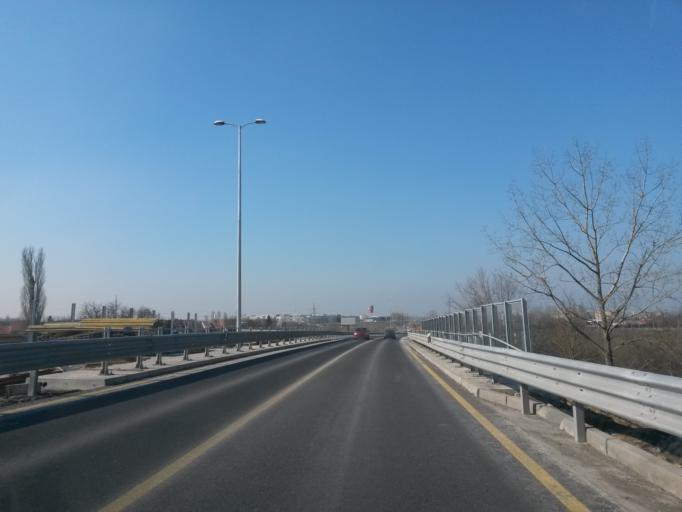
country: HR
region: Osjecko-Baranjska
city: Brijest
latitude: 45.5443
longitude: 18.6694
